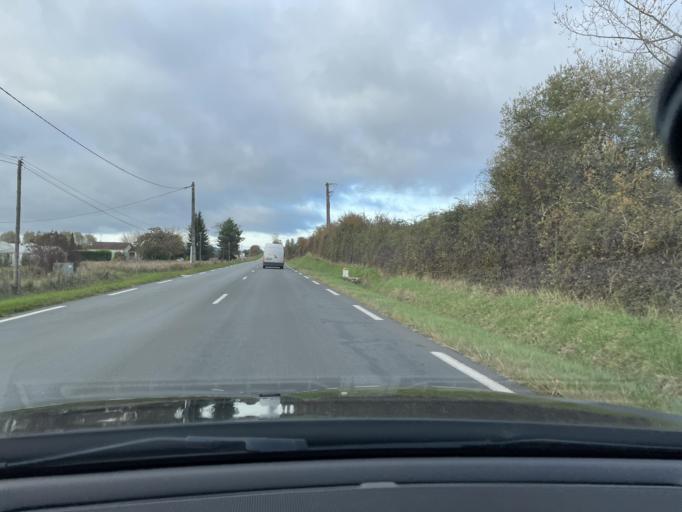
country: FR
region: Aquitaine
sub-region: Departement du Lot-et-Garonne
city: Casteljaloux
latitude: 44.3549
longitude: 0.1073
